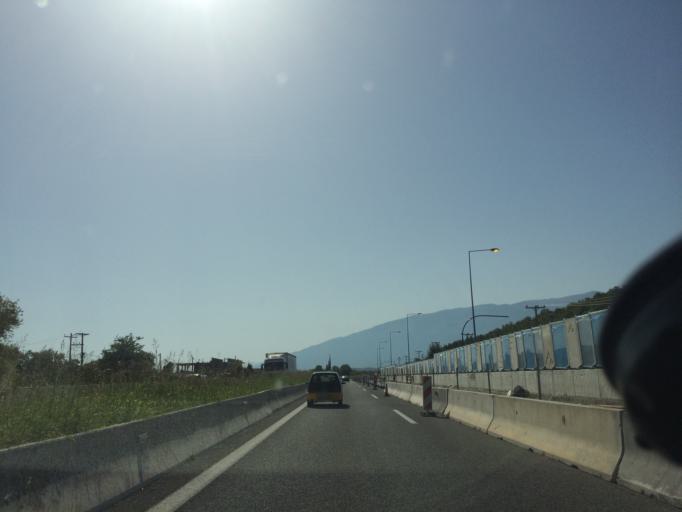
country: GR
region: Thessaly
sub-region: Nomos Larisis
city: Pyrgetos
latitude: 39.9506
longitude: 22.6472
